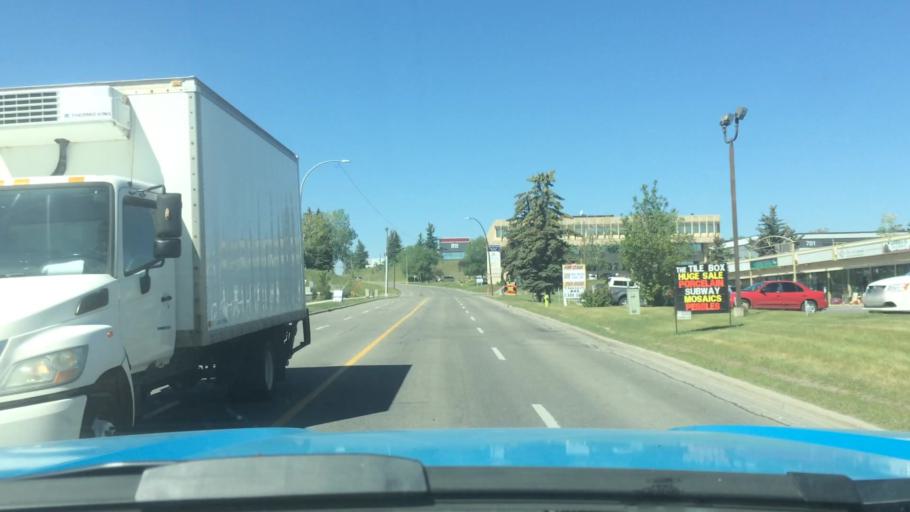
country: CA
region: Alberta
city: Calgary
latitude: 51.0571
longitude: -113.9872
